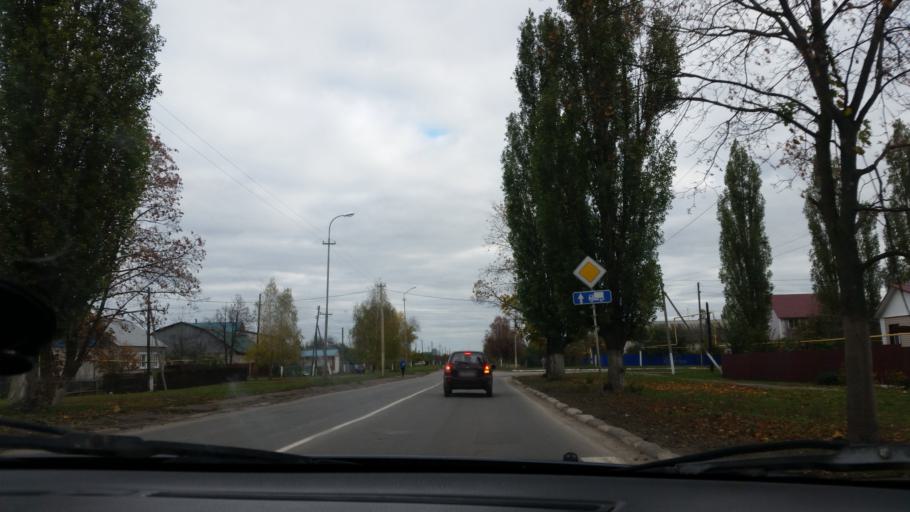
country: RU
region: Lipetsk
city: Gryazi
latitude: 52.4817
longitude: 39.9517
